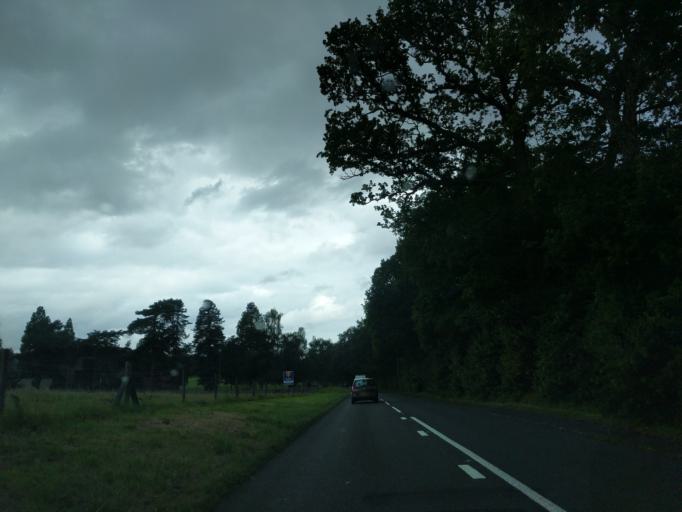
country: GB
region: England
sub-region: Staffordshire
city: Colwich
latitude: 52.7869
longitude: -2.0085
